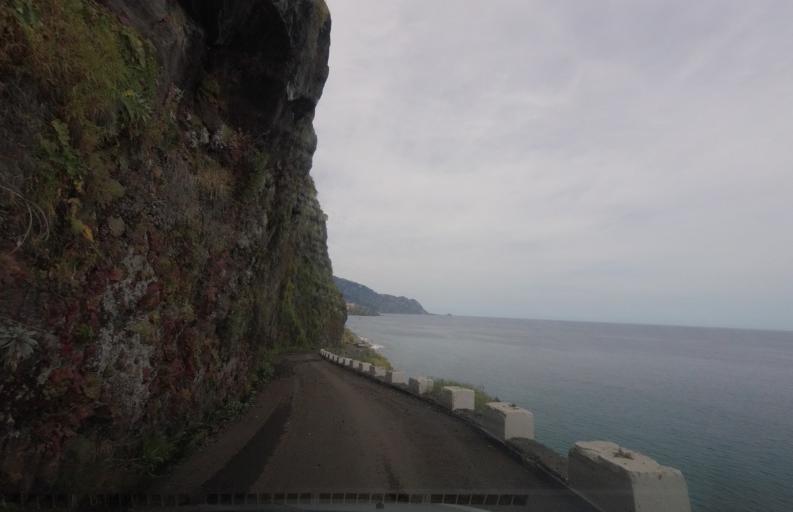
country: PT
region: Madeira
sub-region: Sao Vicente
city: Sao Vicente
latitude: 32.8135
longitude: -17.0749
